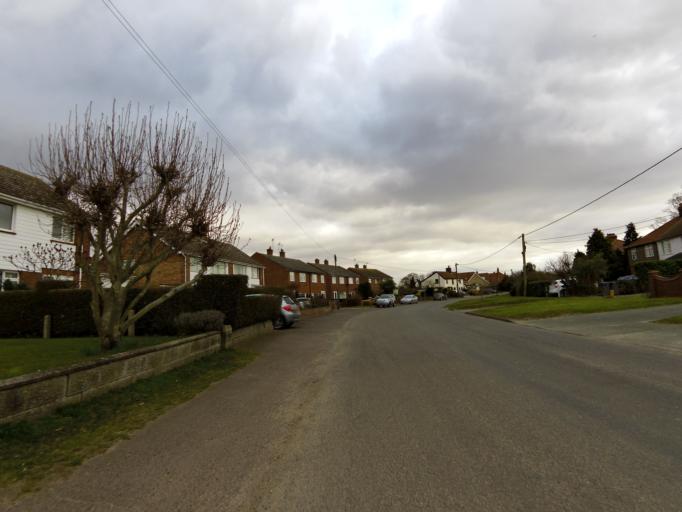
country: GB
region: England
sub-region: Suffolk
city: Felixstowe
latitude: 52.0140
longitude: 1.3127
